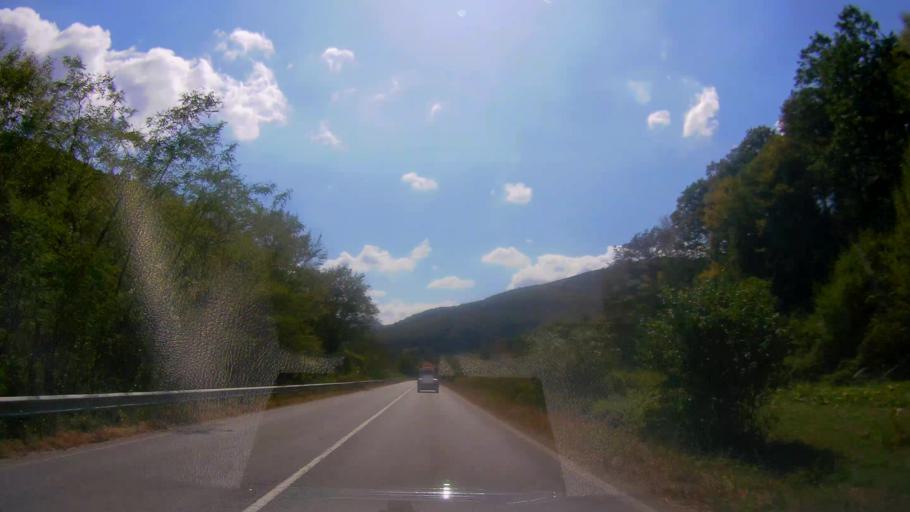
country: BG
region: Stara Zagora
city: Gurkovo
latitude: 42.7435
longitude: 25.7093
